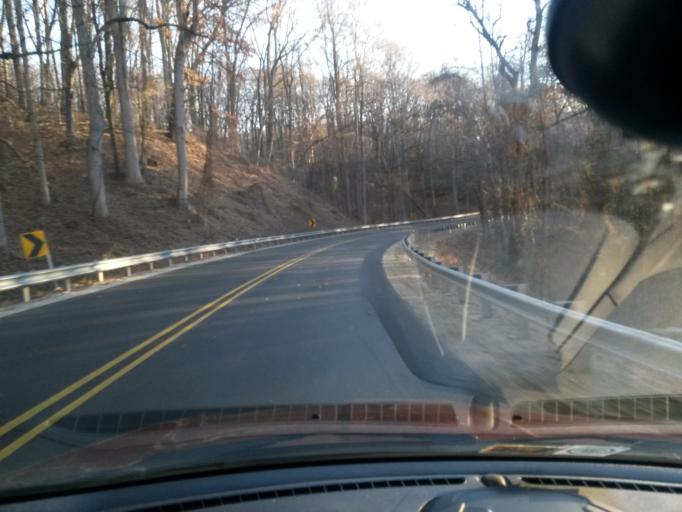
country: US
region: Virginia
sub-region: City of Buena Vista
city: Buena Vista
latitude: 37.7498
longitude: -79.2938
